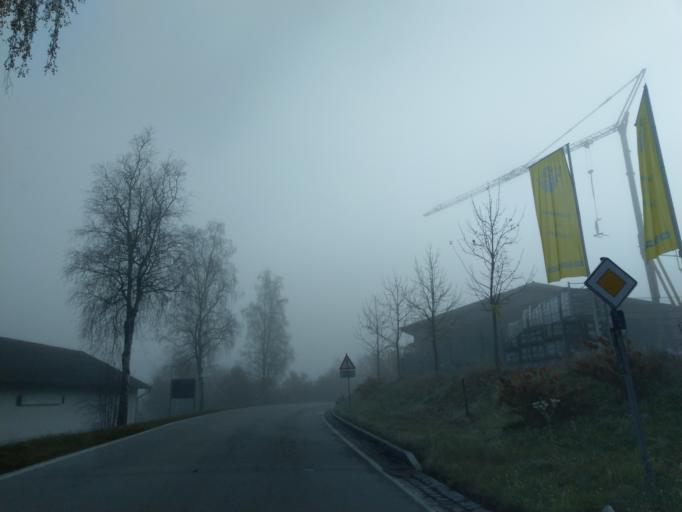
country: DE
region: Bavaria
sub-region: Lower Bavaria
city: Schollnach
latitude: 48.7503
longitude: 13.1827
